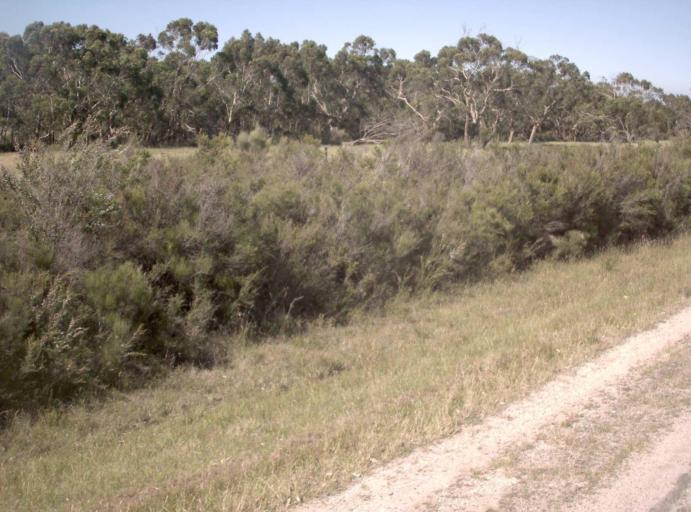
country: AU
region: Victoria
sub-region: Latrobe
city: Morwell
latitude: -38.6355
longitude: 146.5327
